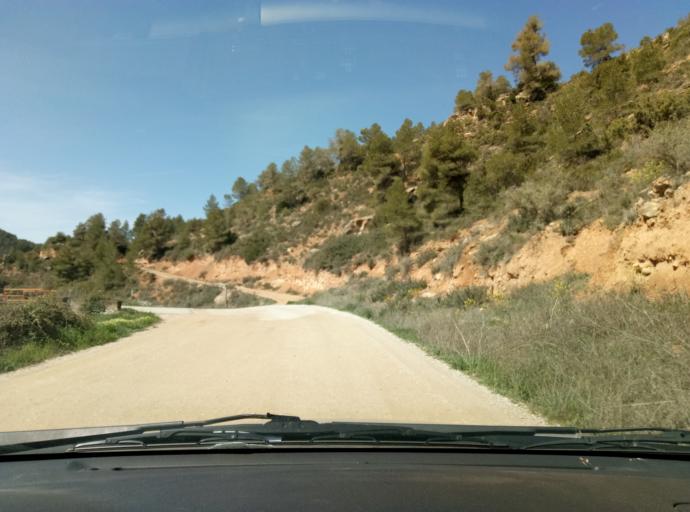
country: ES
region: Catalonia
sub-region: Provincia de Lleida
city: Juncosa
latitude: 41.4239
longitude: 0.8460
